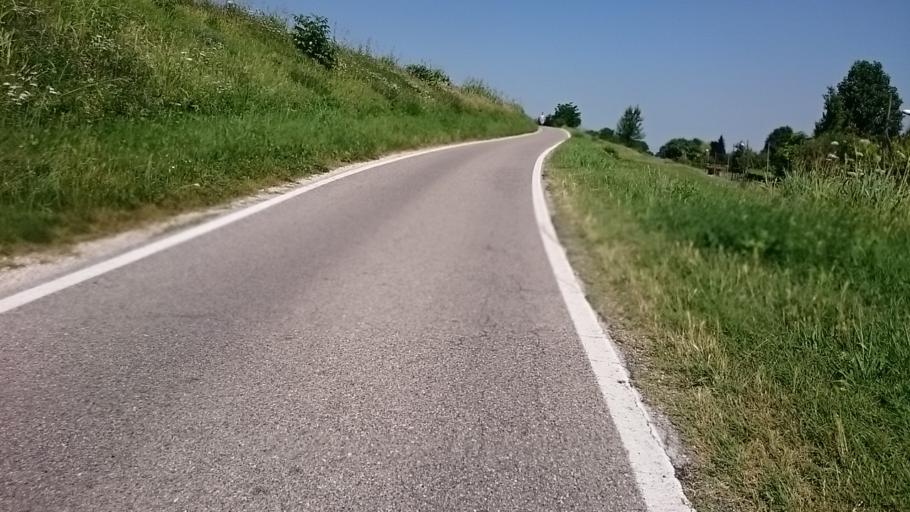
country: IT
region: Veneto
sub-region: Provincia di Venezia
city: Galta
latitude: 45.3728
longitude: 12.0289
